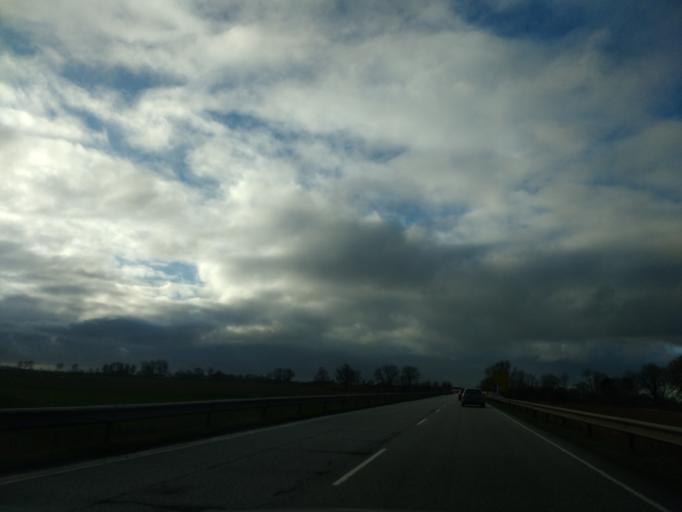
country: DE
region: Schleswig-Holstein
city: Bekmunde
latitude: 53.9370
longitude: 9.4386
